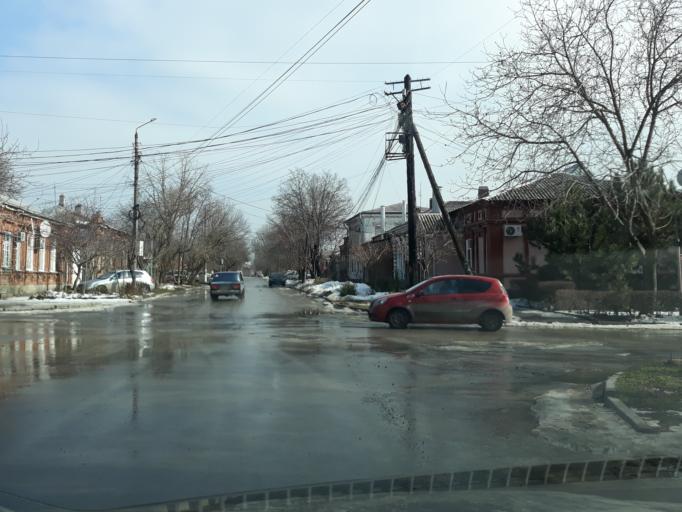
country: RU
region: Rostov
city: Taganrog
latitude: 47.2064
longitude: 38.9289
